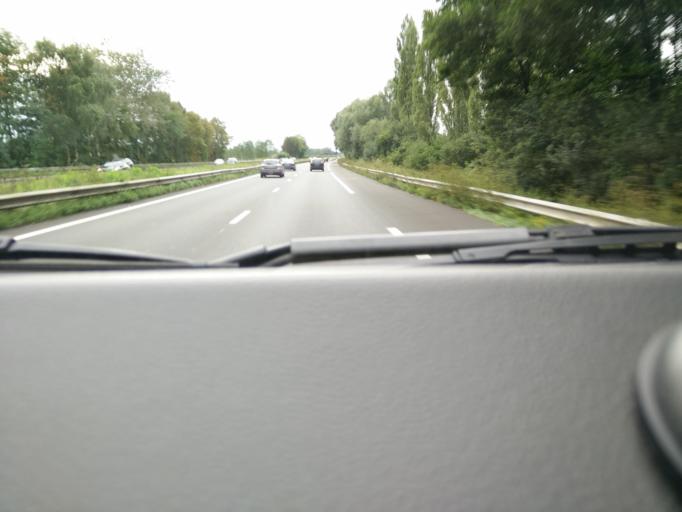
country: FR
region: Nord-Pas-de-Calais
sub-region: Departement du Nord
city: Landas
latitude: 50.4562
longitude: 3.2937
